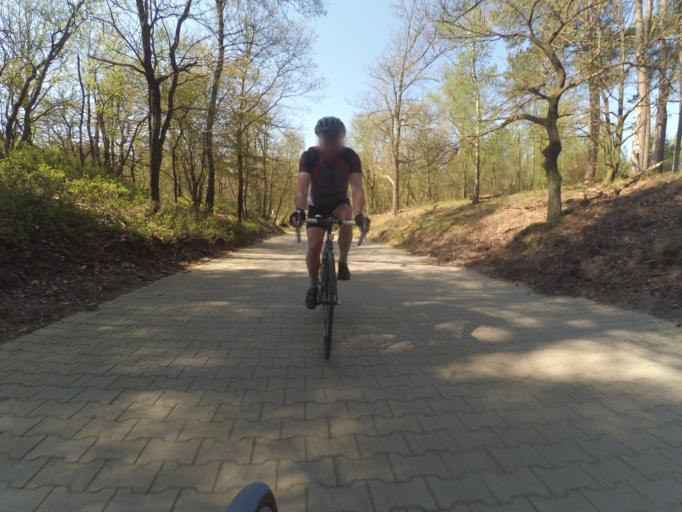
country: NL
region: Gelderland
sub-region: Gemeente Apeldoorn
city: Beekbergen
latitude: 52.1939
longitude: 5.8815
